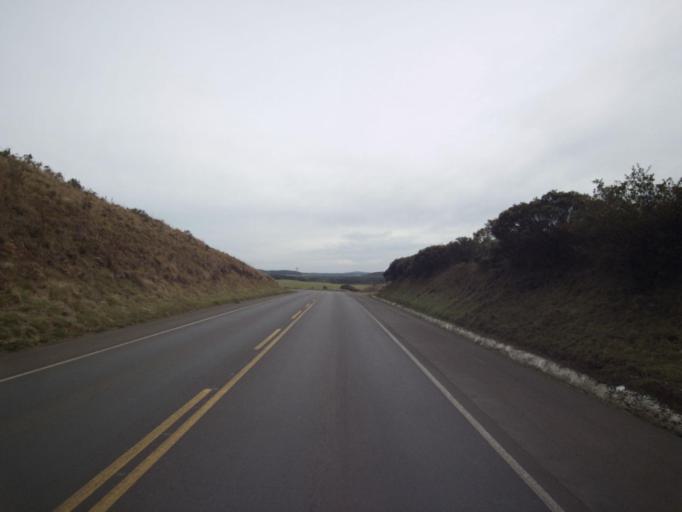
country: BR
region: Parana
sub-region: Palmas
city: Palmas
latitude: -26.6480
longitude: -51.5212
